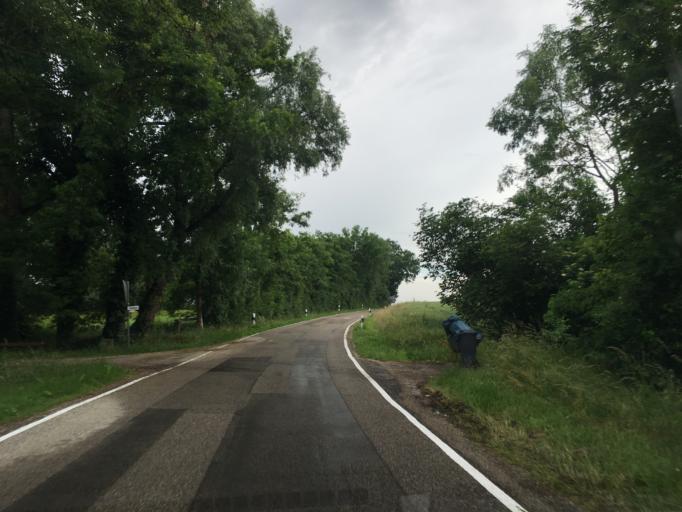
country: DE
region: North Rhine-Westphalia
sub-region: Regierungsbezirk Munster
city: Altenberge
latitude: 52.0330
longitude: 7.4650
